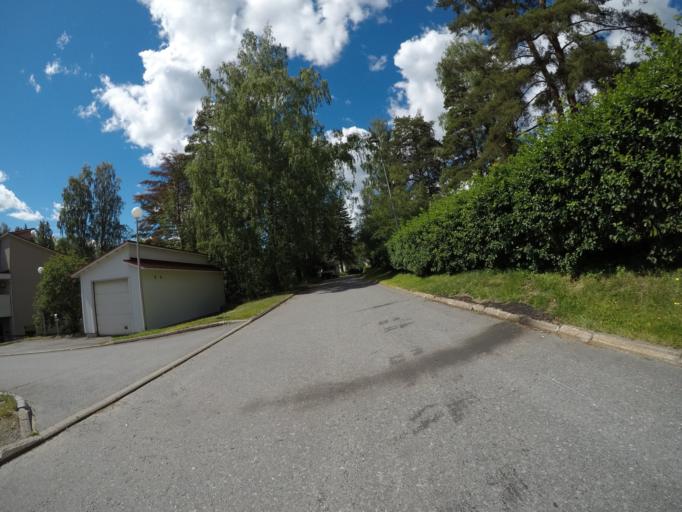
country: FI
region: Haeme
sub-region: Haemeenlinna
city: Haemeenlinna
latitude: 61.0121
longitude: 24.4373
